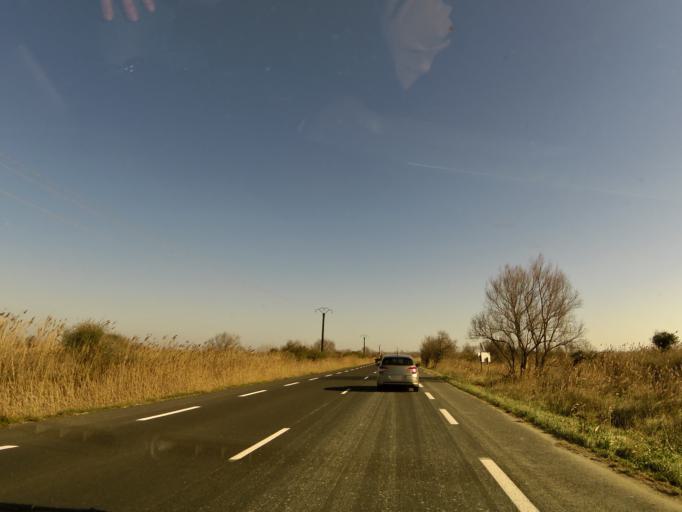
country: FR
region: Provence-Alpes-Cote d'Azur
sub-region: Departement des Bouches-du-Rhone
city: Saintes-Maries-de-la-Mer
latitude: 43.5528
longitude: 4.3312
